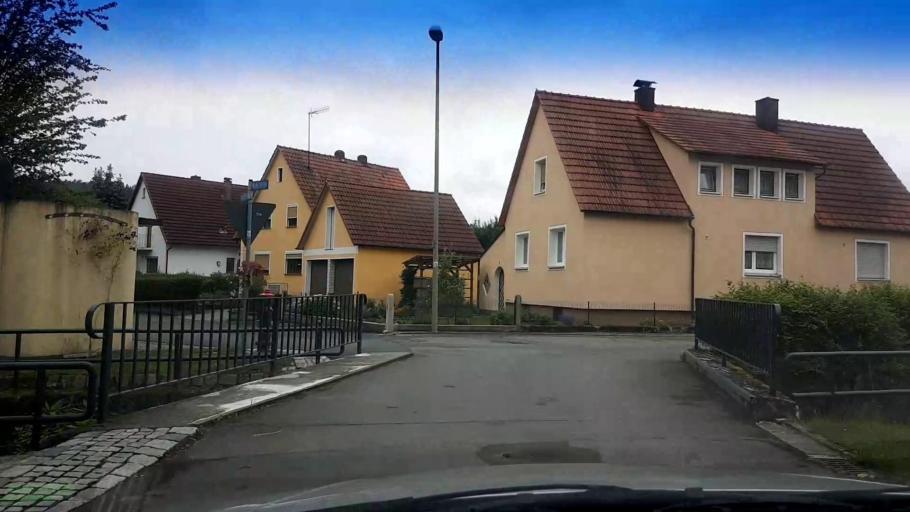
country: DE
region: Bavaria
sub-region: Upper Franconia
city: Mainleus
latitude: 50.0820
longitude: 11.3408
